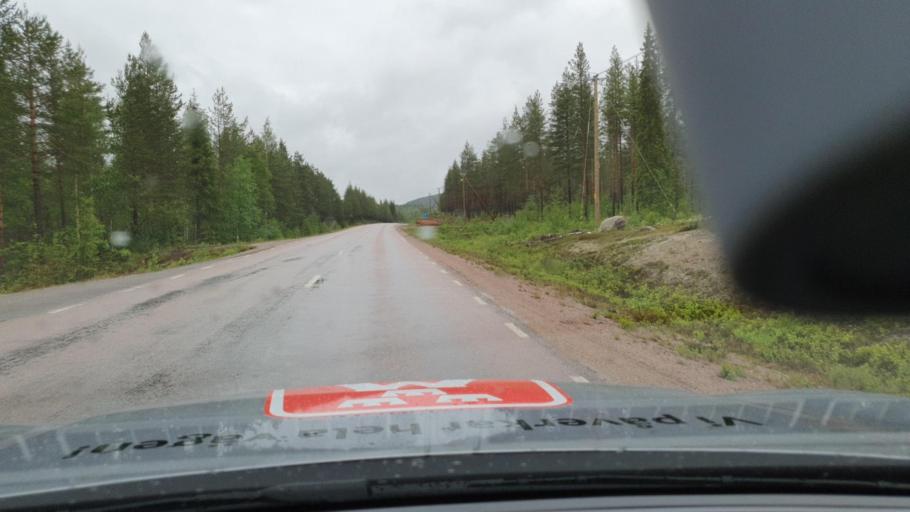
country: SE
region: Norrbotten
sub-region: Overkalix Kommun
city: OEverkalix
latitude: 66.4057
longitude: 22.9548
